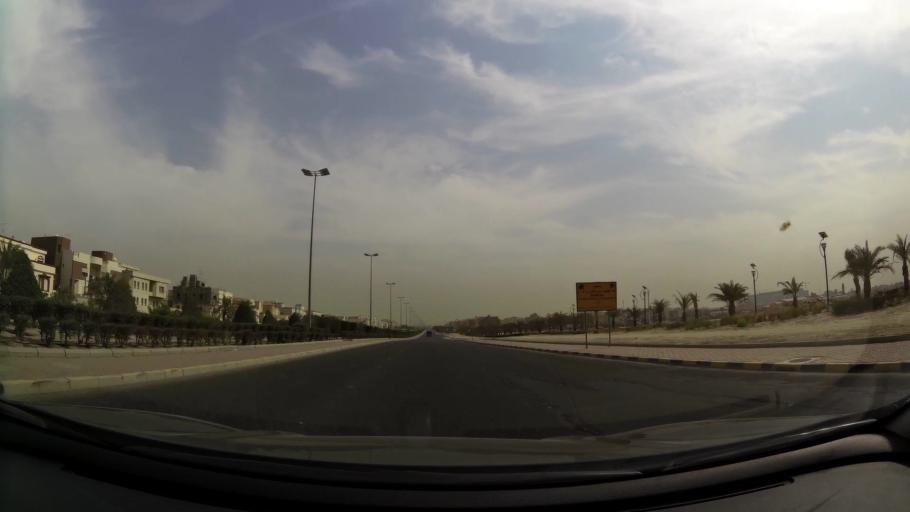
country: KW
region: Al Farwaniyah
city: Janub as Surrah
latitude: 29.2898
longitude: 48.0043
